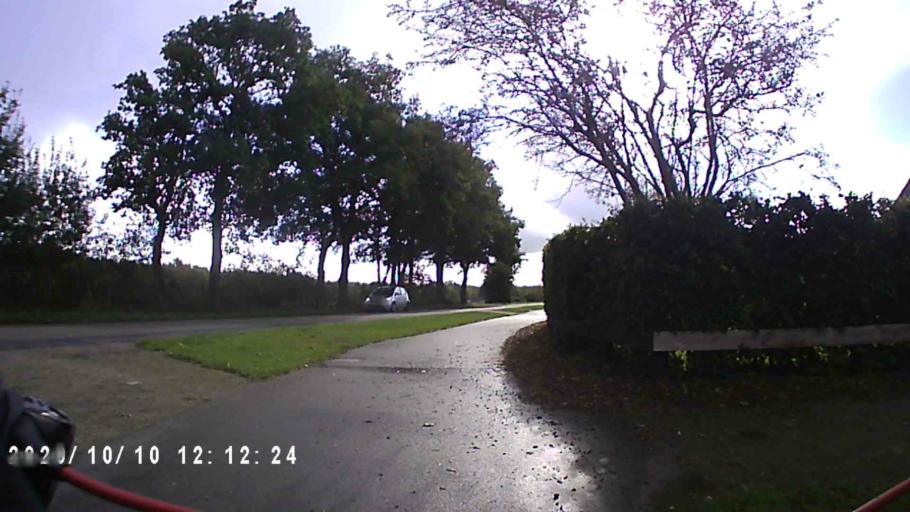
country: NL
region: Friesland
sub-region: Gemeente Heerenveen
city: Jubbega
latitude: 53.0364
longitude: 6.1530
